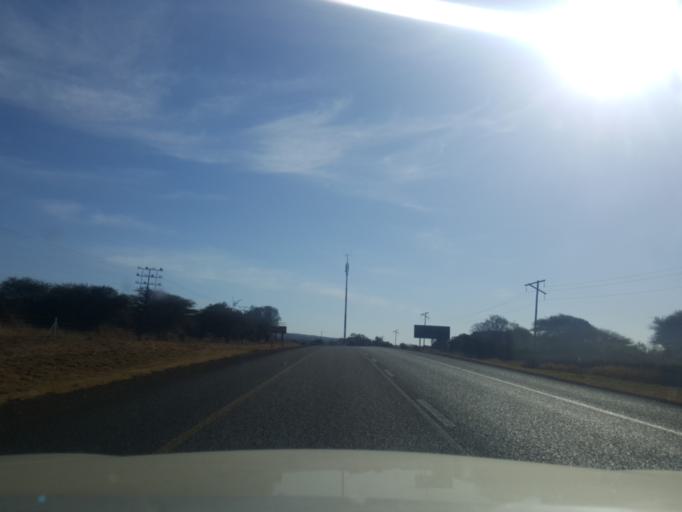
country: ZA
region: North-West
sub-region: Ngaka Modiri Molema District Municipality
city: Zeerust
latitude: -25.5185
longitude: 26.1699
